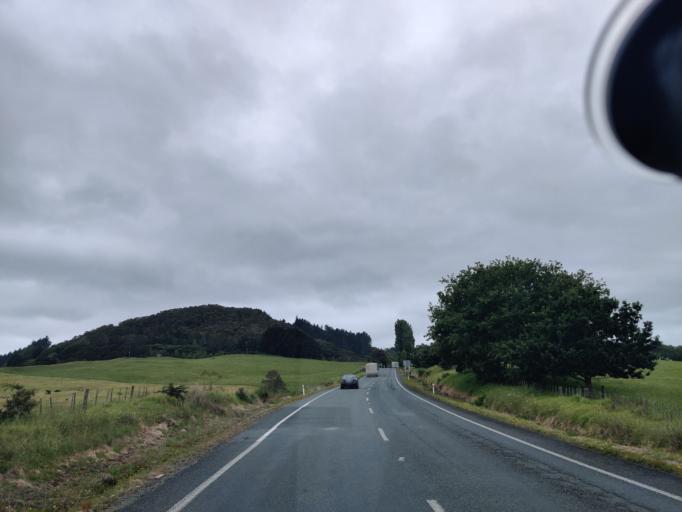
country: NZ
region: Northland
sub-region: Whangarei
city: Ruakaka
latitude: -36.0980
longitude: 174.4239
